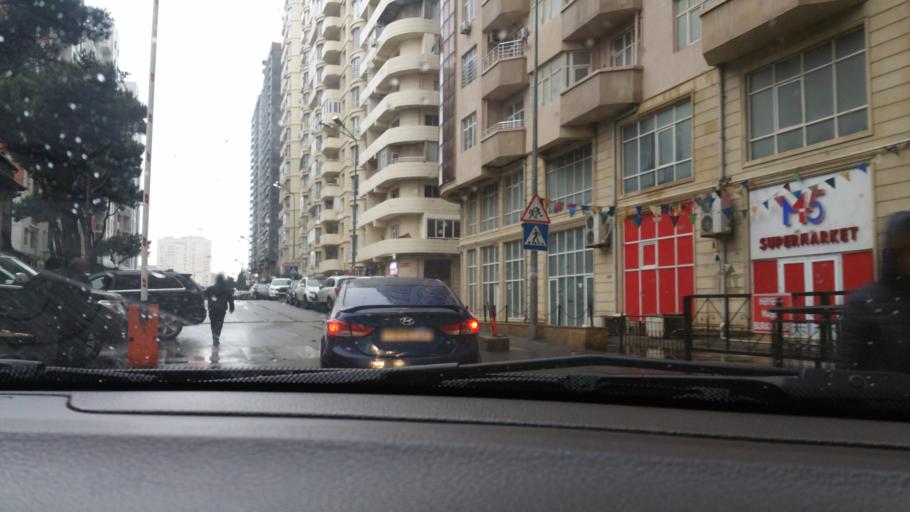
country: AZ
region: Baki
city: Bilajari
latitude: 40.3977
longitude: 49.8189
